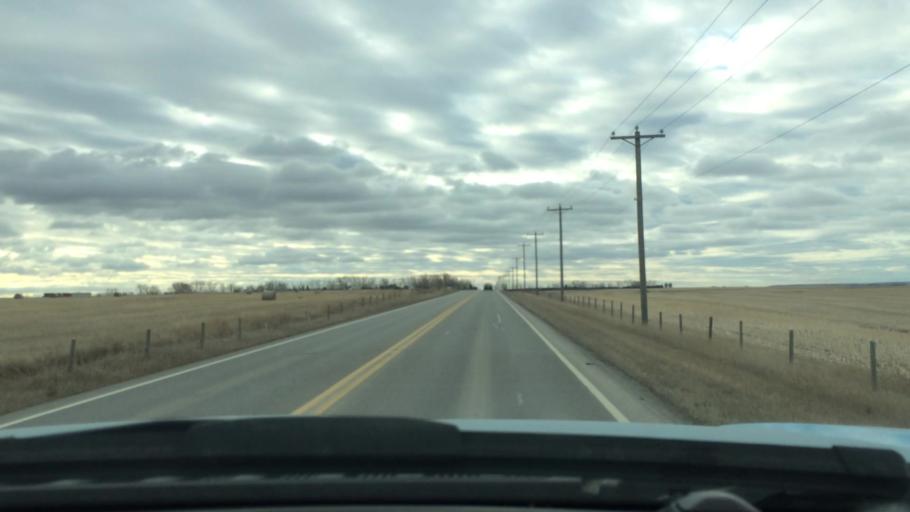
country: CA
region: Alberta
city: Airdrie
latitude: 51.2397
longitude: -114.0250
